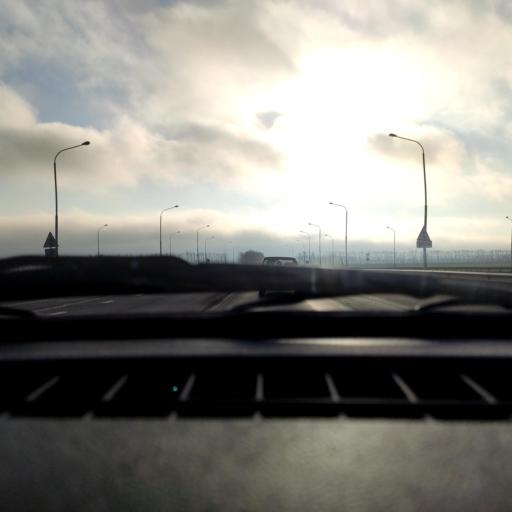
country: RU
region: Bashkortostan
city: Chishmy
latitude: 54.6667
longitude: 55.3997
